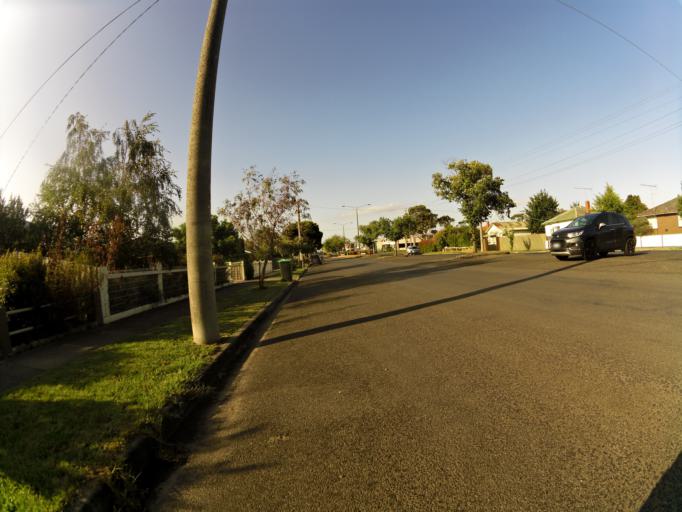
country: AU
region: Victoria
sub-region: Latrobe
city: Morwell
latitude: -38.2402
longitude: 146.3939
